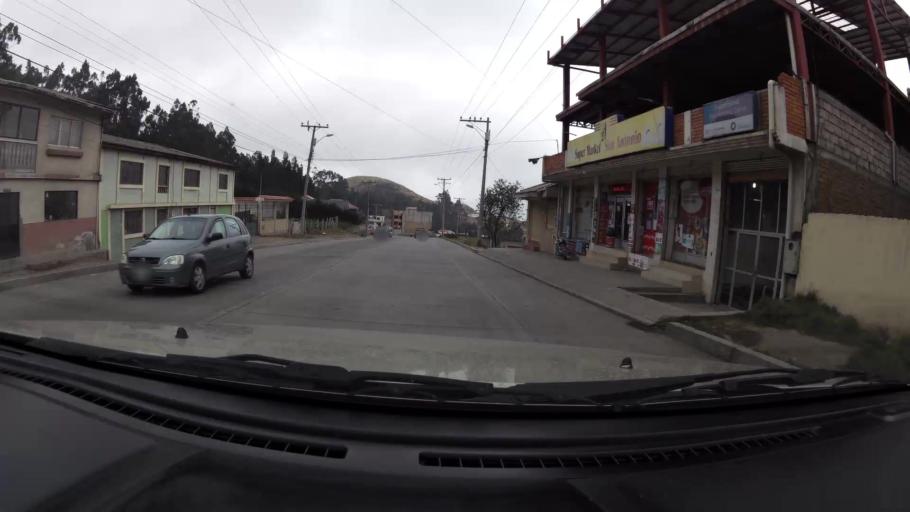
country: EC
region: Canar
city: Canar
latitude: -2.5631
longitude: -78.9421
